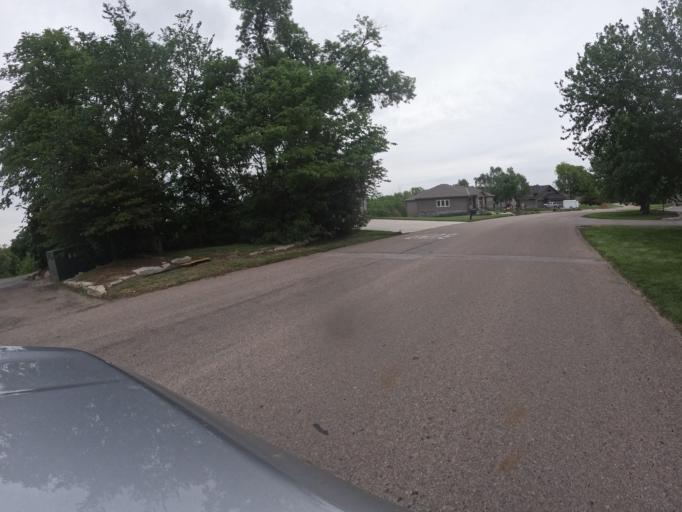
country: US
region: Nebraska
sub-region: Sarpy County
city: Offutt Air Force Base
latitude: 41.0511
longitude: -95.9608
